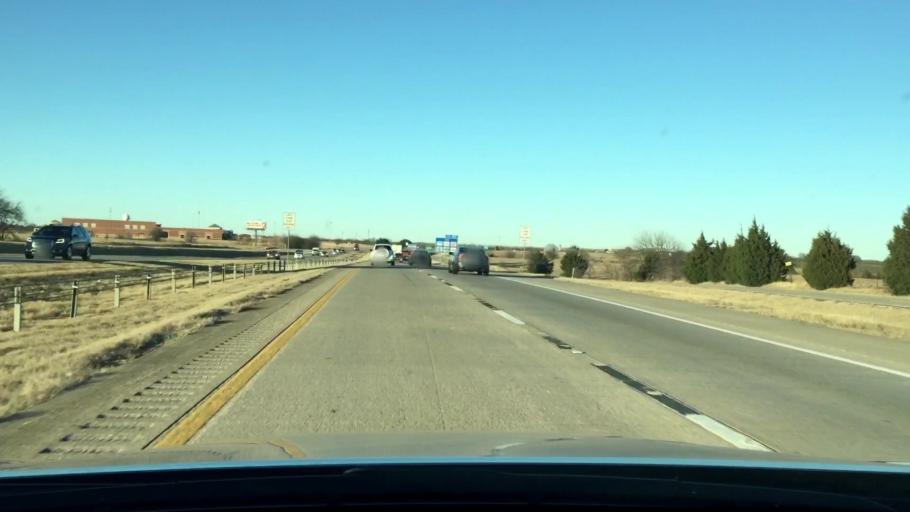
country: US
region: Texas
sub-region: Cooke County
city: Gainesville
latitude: 33.5967
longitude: -97.1618
